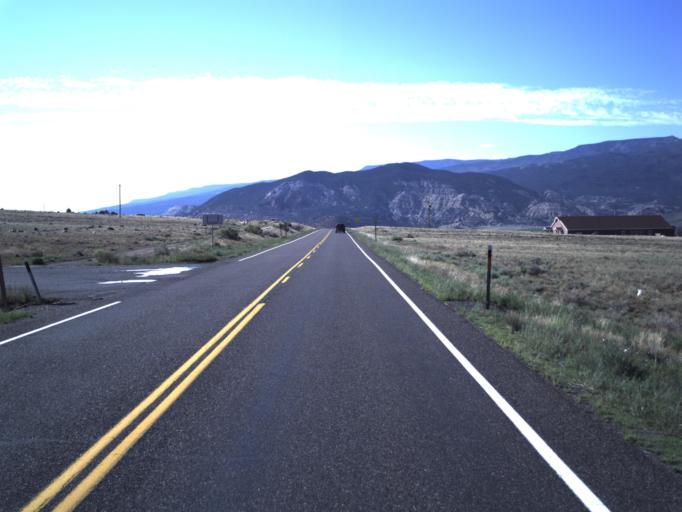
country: US
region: Utah
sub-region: Wayne County
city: Loa
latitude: 38.3346
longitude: -111.5371
